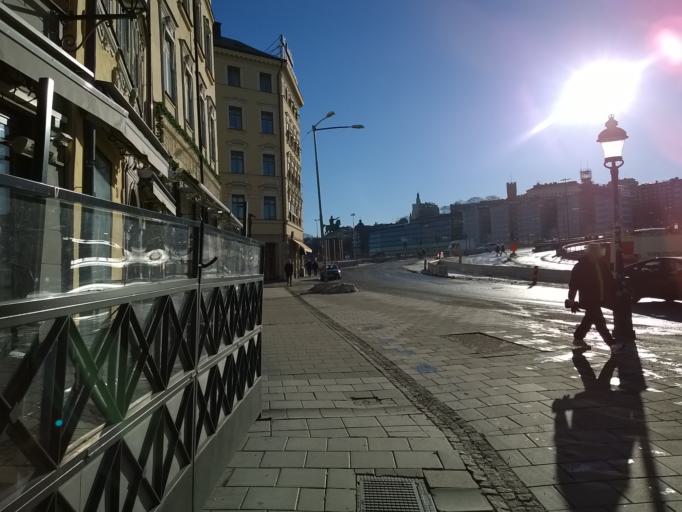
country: SE
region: Stockholm
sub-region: Stockholms Kommun
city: Stockholm
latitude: 59.3226
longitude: 18.0718
